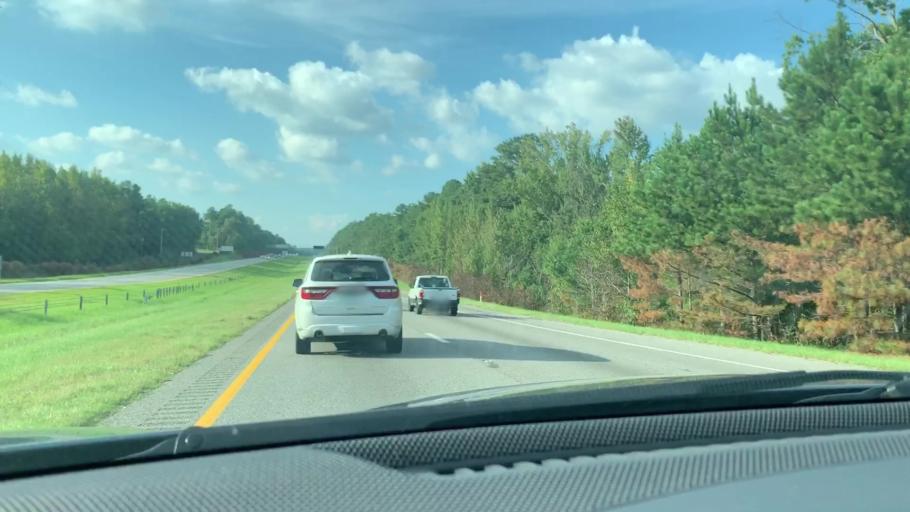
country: US
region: South Carolina
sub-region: Calhoun County
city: Oak Grove
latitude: 33.6767
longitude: -80.9006
